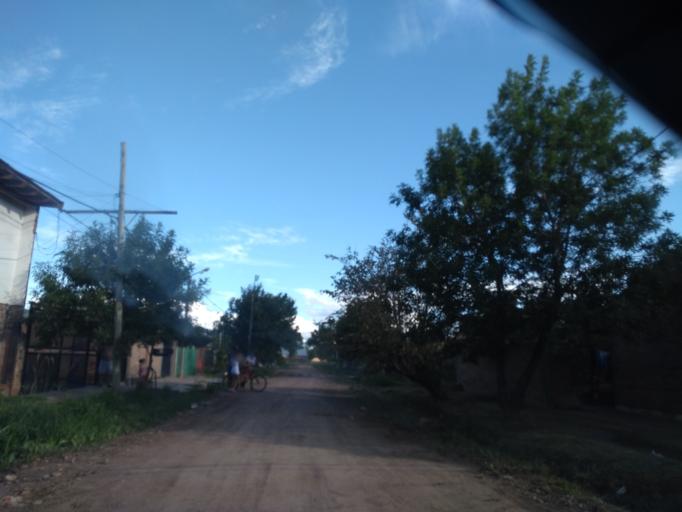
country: AR
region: Chaco
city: Fontana
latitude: -27.4139
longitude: -59.0419
